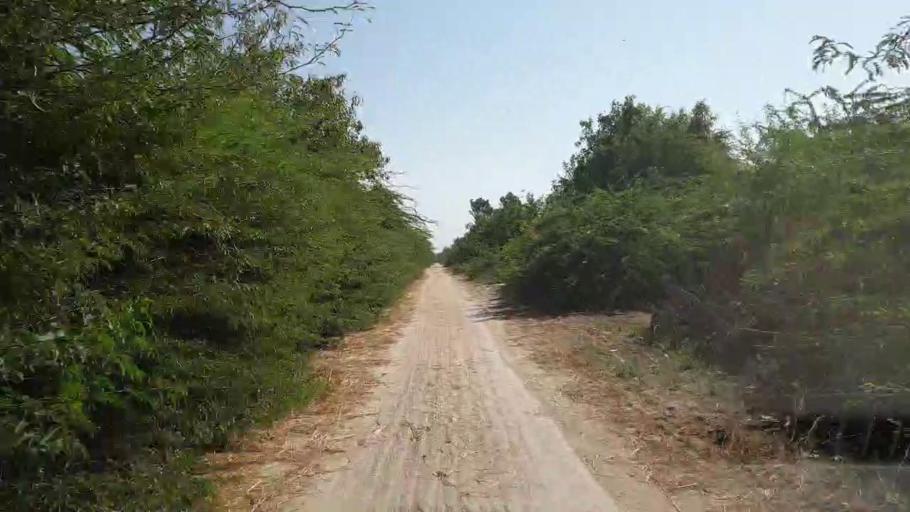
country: PK
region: Sindh
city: Tando Bago
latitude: 24.6551
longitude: 68.9810
